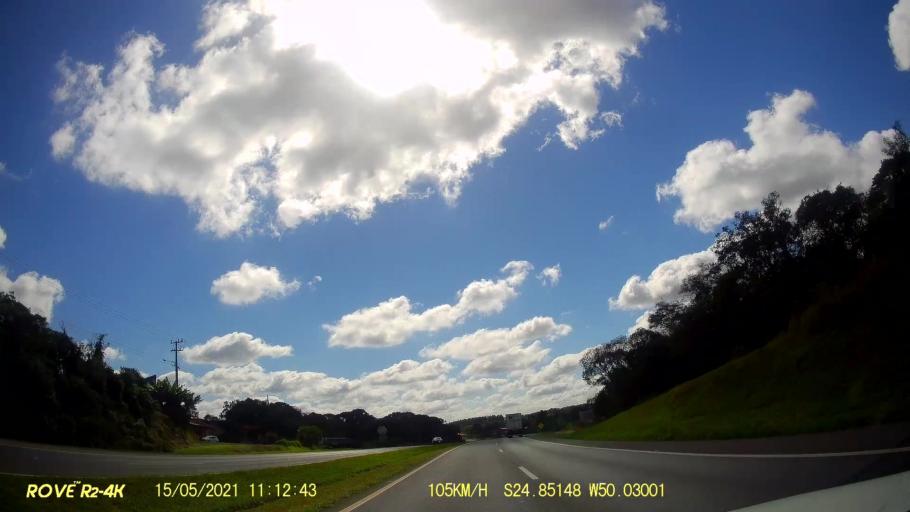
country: BR
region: Parana
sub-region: Castro
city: Castro
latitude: -24.8518
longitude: -50.0302
